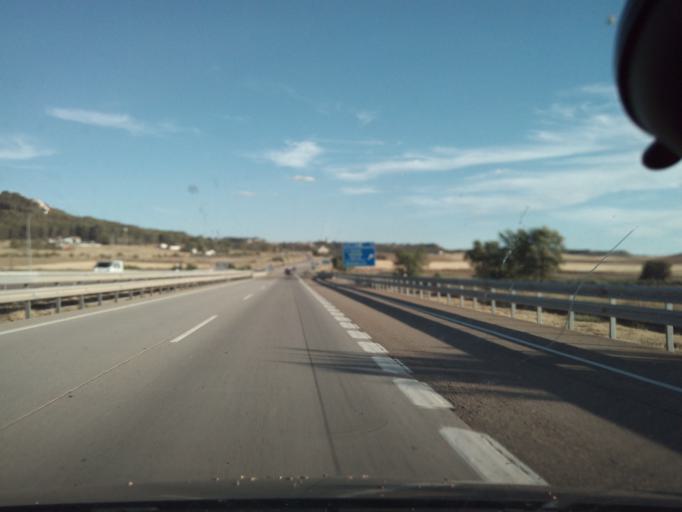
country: ES
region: Castille-La Mancha
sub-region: Province of Toledo
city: Dosbarrios
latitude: 39.8110
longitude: -3.4793
